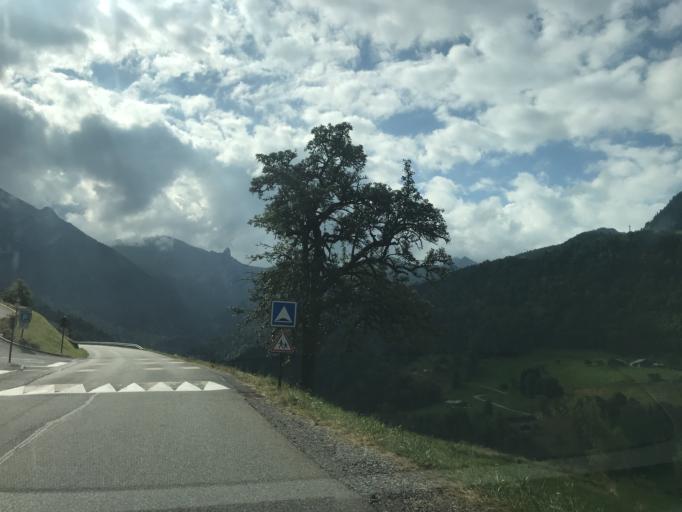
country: FR
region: Rhone-Alpes
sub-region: Departement de la Haute-Savoie
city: Thones
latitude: 45.8601
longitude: 6.3714
